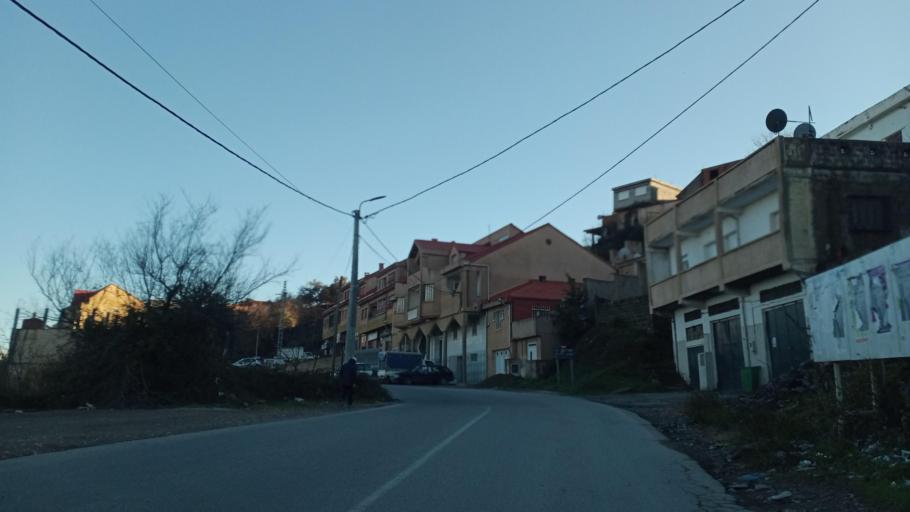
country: DZ
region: Tizi Ouzou
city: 'Ain el Hammam
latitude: 36.5600
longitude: 4.3241
